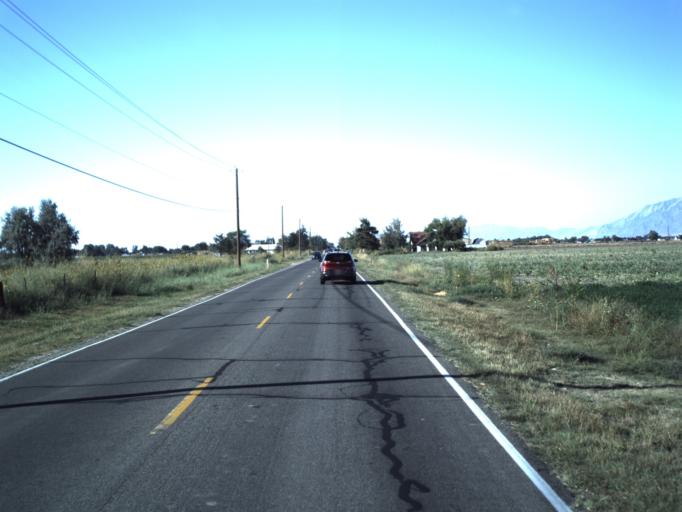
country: US
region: Utah
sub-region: Weber County
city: Hooper
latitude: 41.1440
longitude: -112.1229
